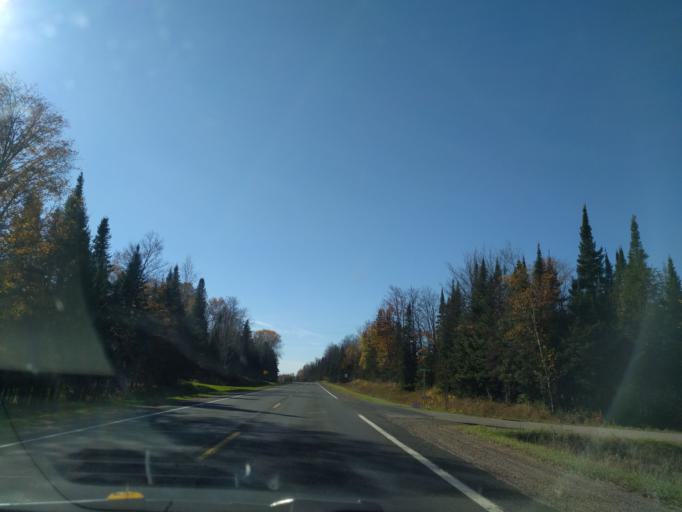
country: US
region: Michigan
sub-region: Iron County
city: Crystal Falls
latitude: 46.1715
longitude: -88.0623
